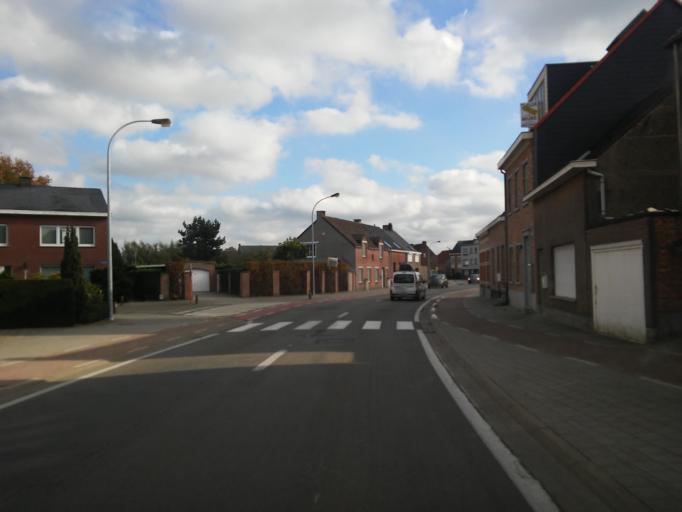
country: BE
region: Flanders
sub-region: Provincie Antwerpen
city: Berlaar
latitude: 51.1179
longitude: 4.6447
